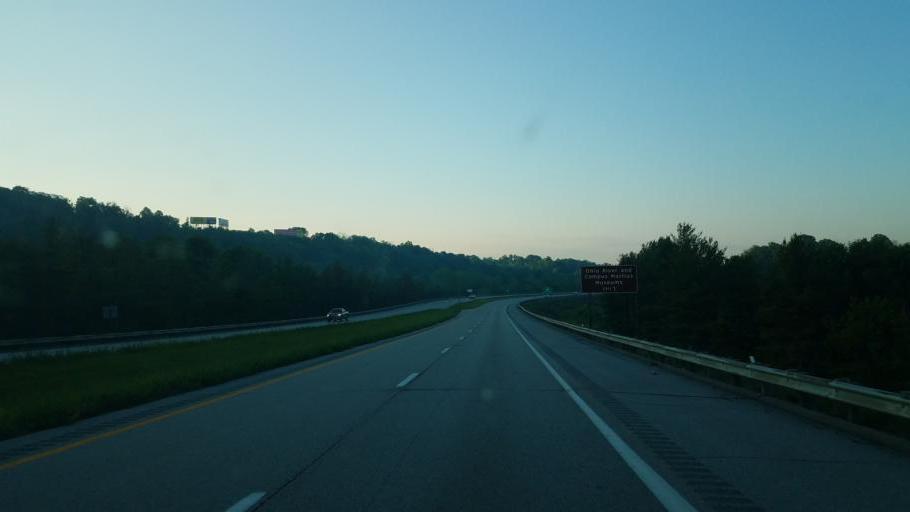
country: US
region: Ohio
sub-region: Washington County
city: Marietta
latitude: 39.4203
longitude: -81.4248
